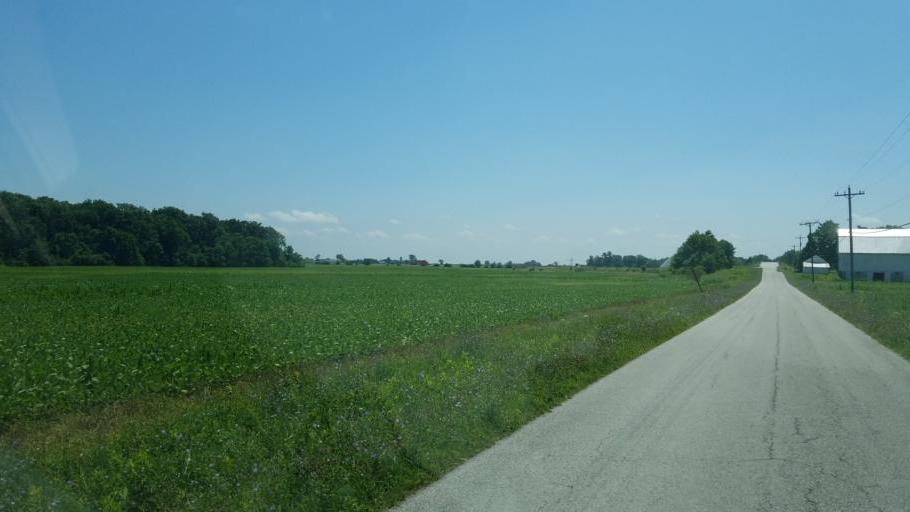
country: US
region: Ohio
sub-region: Sandusky County
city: Fremont
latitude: 41.3993
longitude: -83.0873
